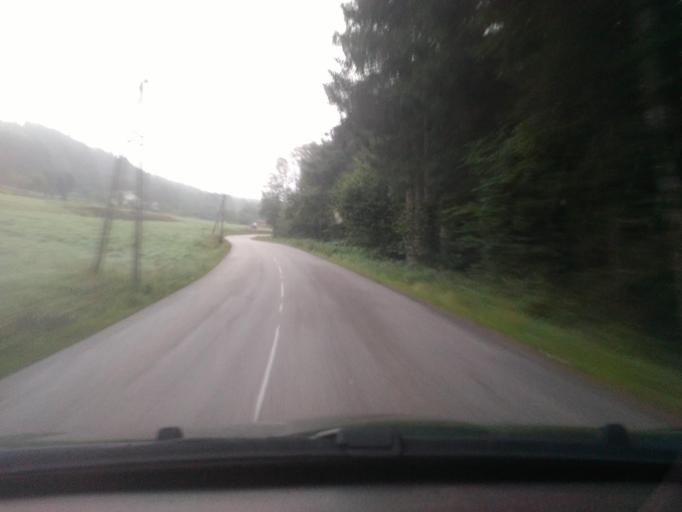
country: FR
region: Lorraine
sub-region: Departement des Vosges
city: Granges-sur-Vologne
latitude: 48.1428
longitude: 6.8299
